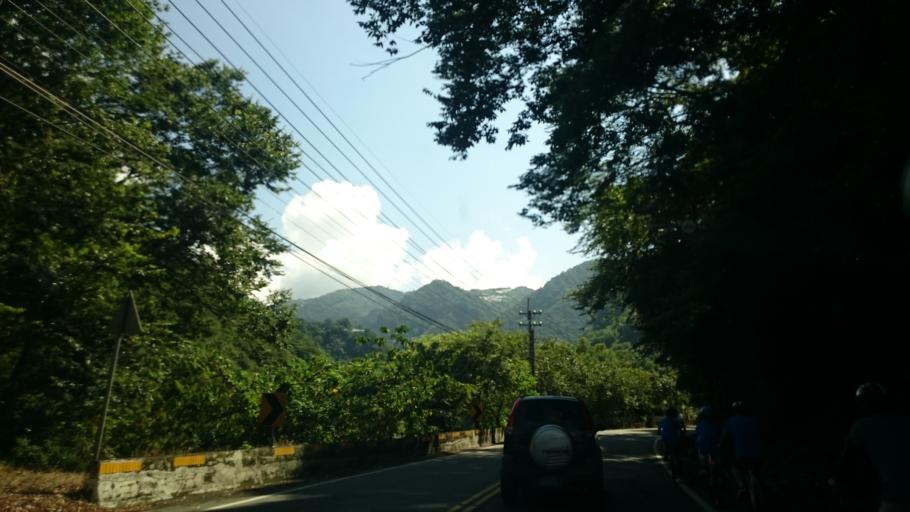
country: TW
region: Taiwan
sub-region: Nantou
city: Puli
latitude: 24.0074
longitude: 121.0948
